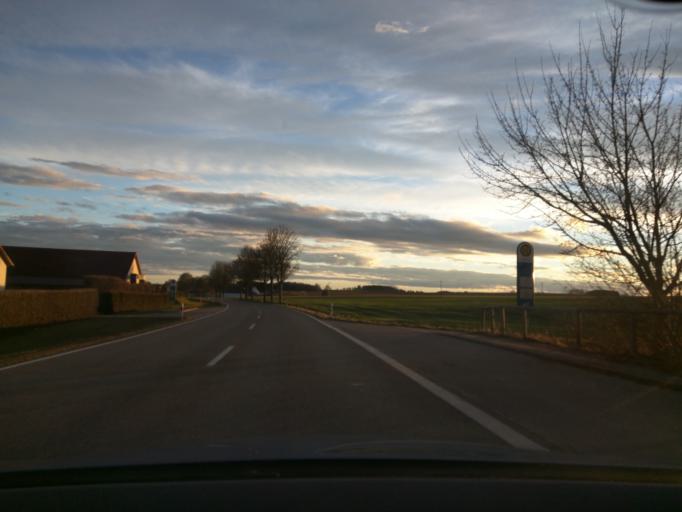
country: DE
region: Bavaria
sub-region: Upper Bavaria
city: Attenkirchen
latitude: 48.4852
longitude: 11.7601
